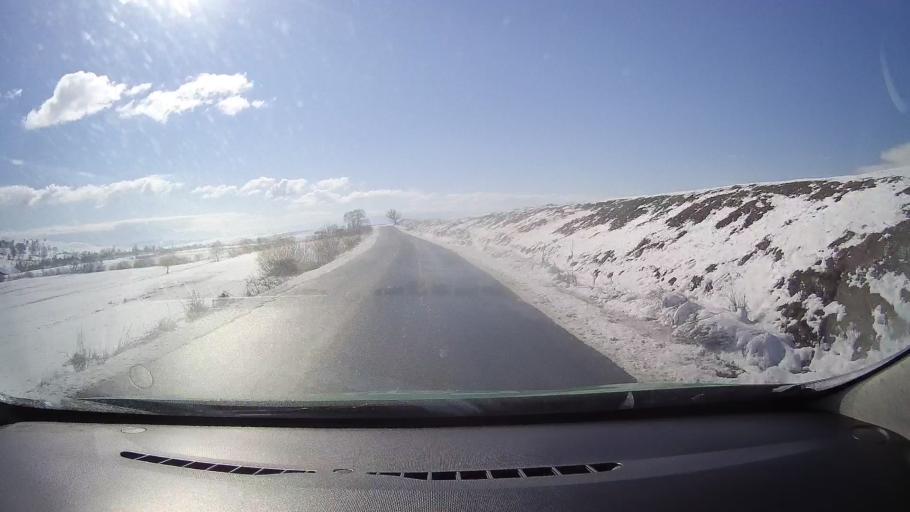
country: RO
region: Sibiu
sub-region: Comuna Rosia
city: Rosia
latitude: 45.8562
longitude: 24.3109
